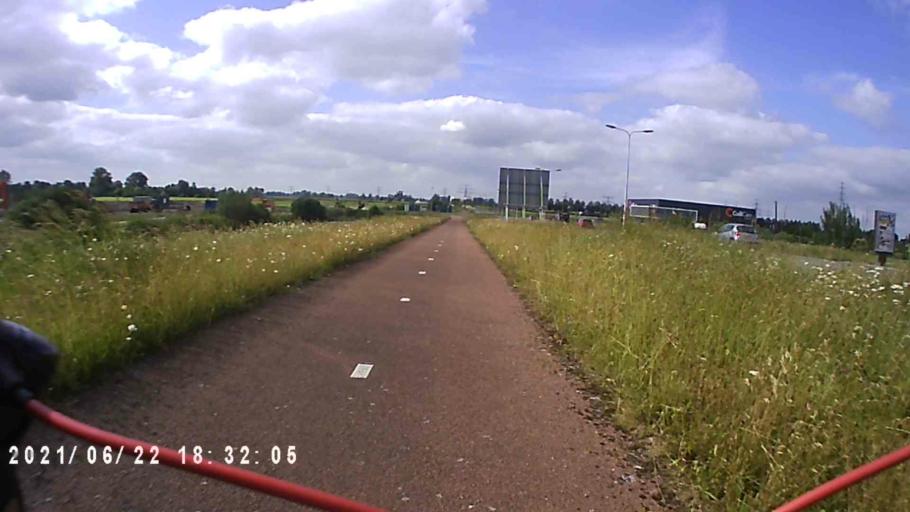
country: NL
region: Groningen
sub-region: Gemeente Zuidhorn
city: Aduard
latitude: 53.2038
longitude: 6.4730
